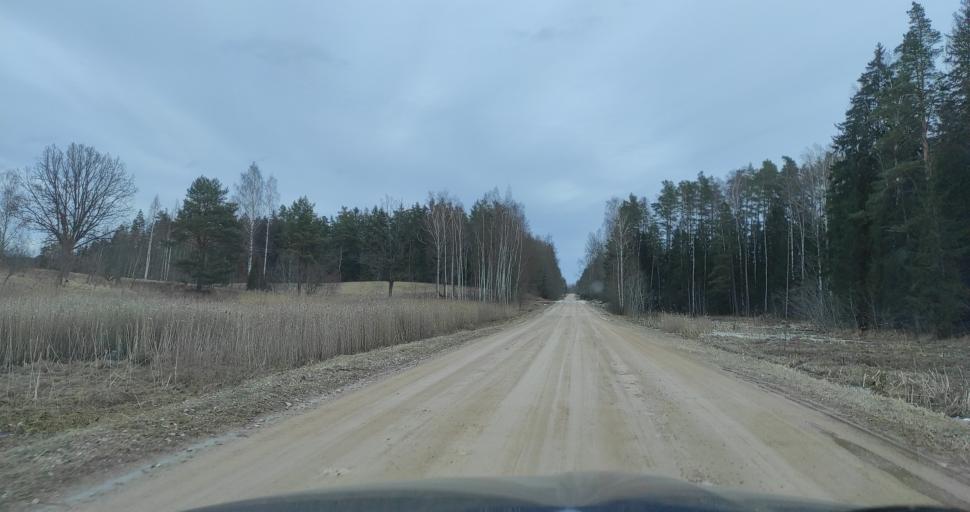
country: LV
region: Tukuma Rajons
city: Tukums
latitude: 57.0802
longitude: 23.0718
